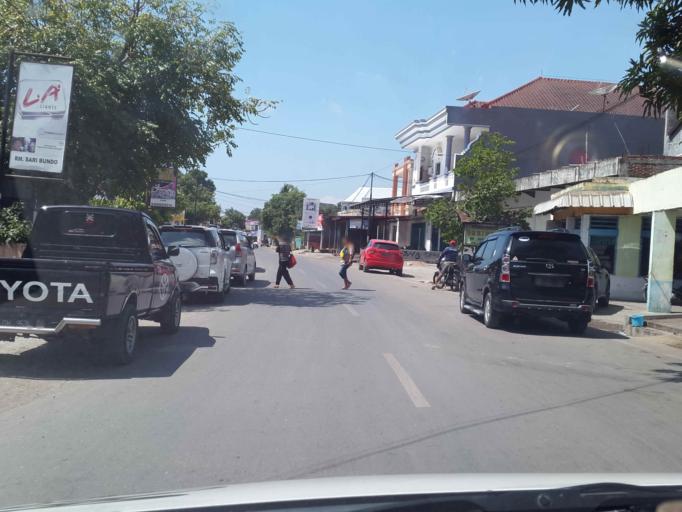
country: ID
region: East Nusa Tenggara
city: Atambua
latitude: -9.1065
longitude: 124.8951
